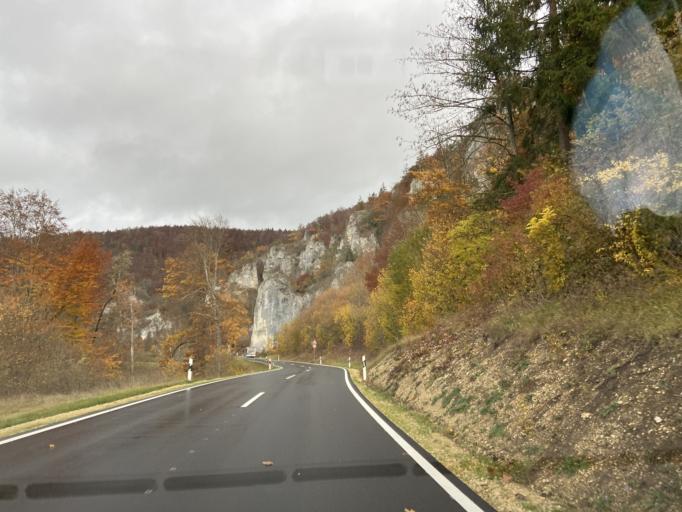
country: DE
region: Baden-Wuerttemberg
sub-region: Tuebingen Region
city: Stetten am Kalten Markt
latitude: 48.0902
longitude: 9.1086
